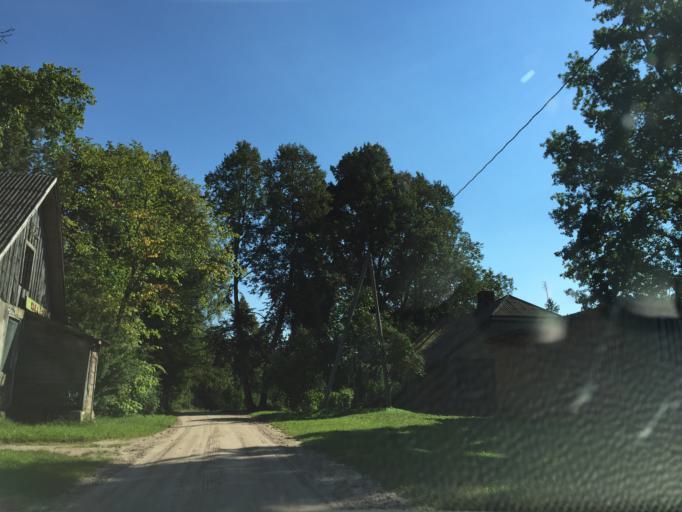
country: LV
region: Limbazu Rajons
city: Limbazi
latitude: 57.5514
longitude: 24.7705
